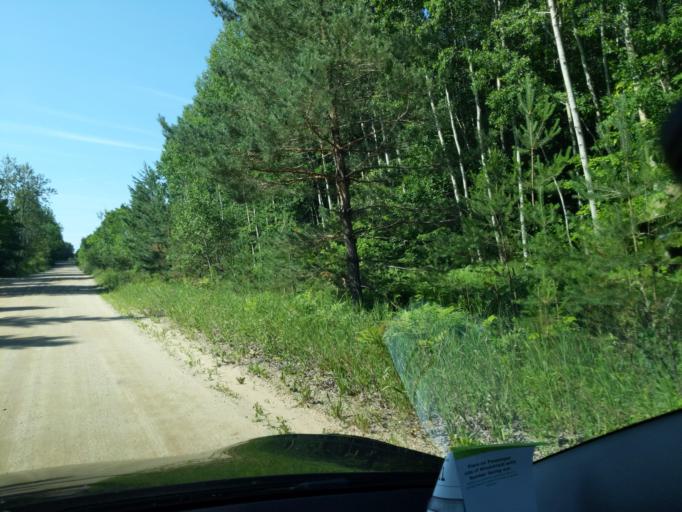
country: US
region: Michigan
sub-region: Cheboygan County
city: Cheboygan
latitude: 45.6754
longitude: -84.6508
